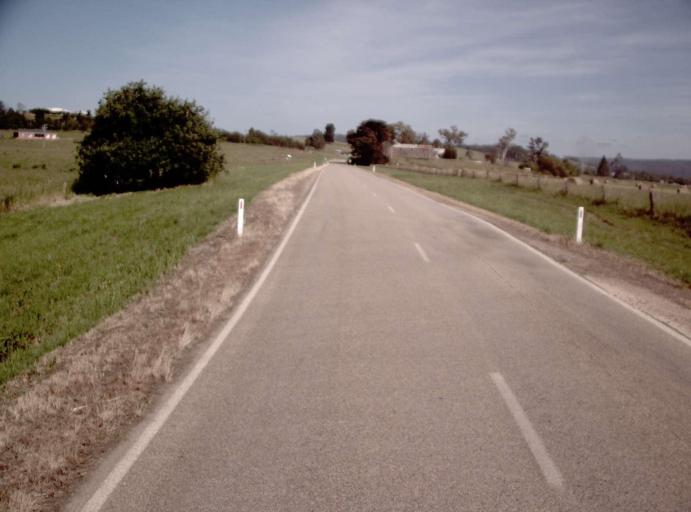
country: AU
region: Victoria
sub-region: East Gippsland
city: Lakes Entrance
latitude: -37.7398
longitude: 147.8177
